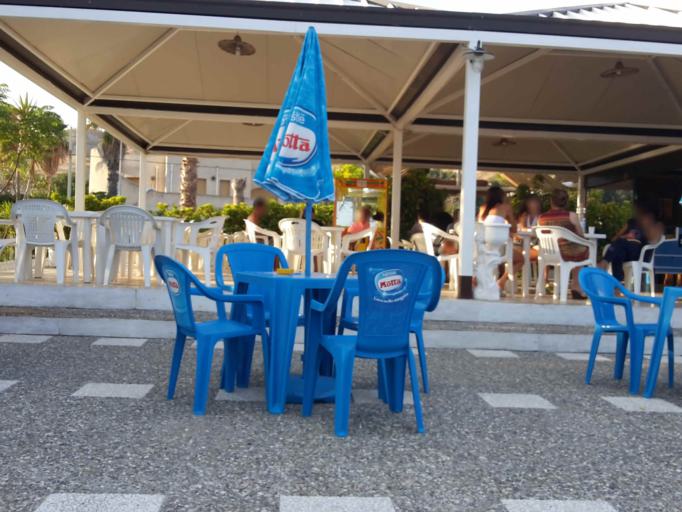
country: IT
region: Calabria
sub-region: Provincia di Reggio Calabria
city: San Carlo-Condofuri Marina
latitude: 37.9190
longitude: 15.8307
